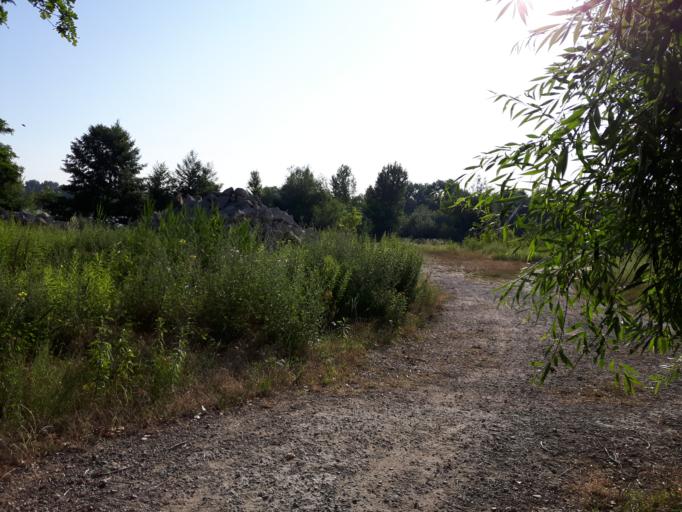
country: DE
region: Baden-Wuerttemberg
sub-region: Karlsruhe Region
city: Karlsdorf-Neuthard
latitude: 49.0958
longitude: 8.5322
